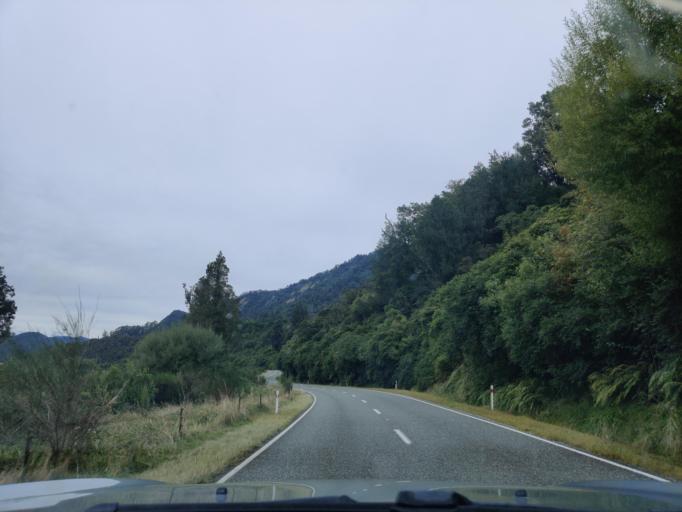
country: NZ
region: West Coast
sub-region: Buller District
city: Westport
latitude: -41.8570
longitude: 171.8742
